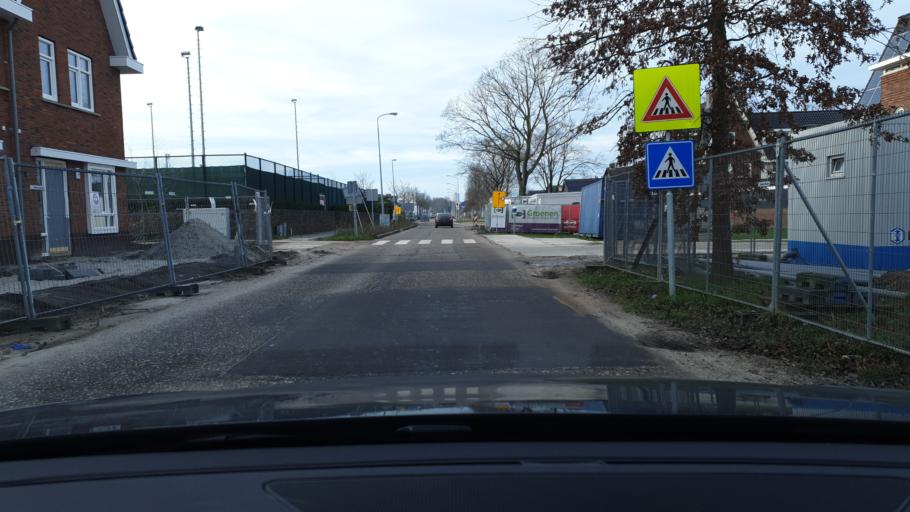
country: NL
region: North Brabant
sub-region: Gemeente Eindhoven
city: Muschberg en Geestenberg
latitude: 51.4349
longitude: 5.5208
